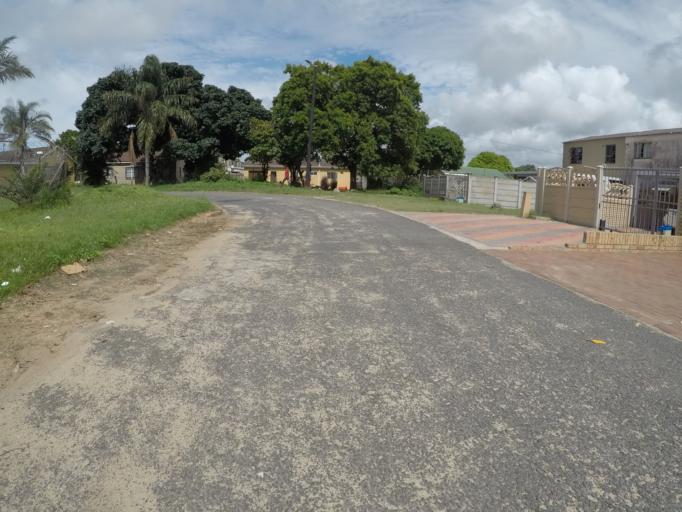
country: ZA
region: KwaZulu-Natal
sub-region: uThungulu District Municipality
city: eSikhawini
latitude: -28.8748
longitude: 31.9093
